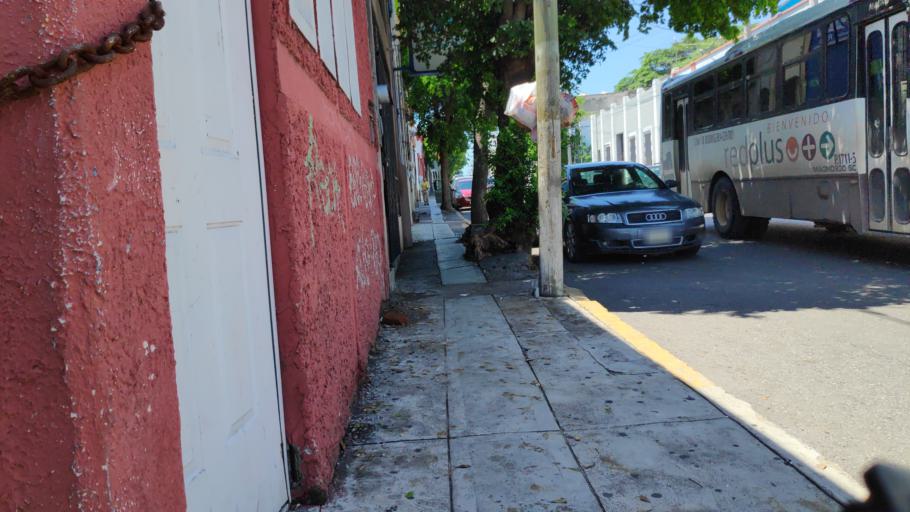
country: MX
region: Sinaloa
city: Culiacan
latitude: 24.8104
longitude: -107.3913
